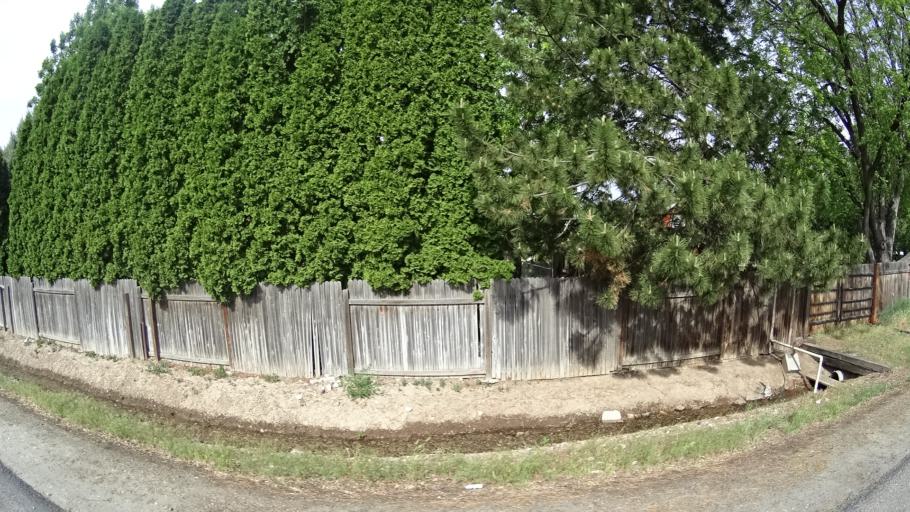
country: US
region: Idaho
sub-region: Ada County
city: Garden City
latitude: 43.5528
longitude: -116.2943
